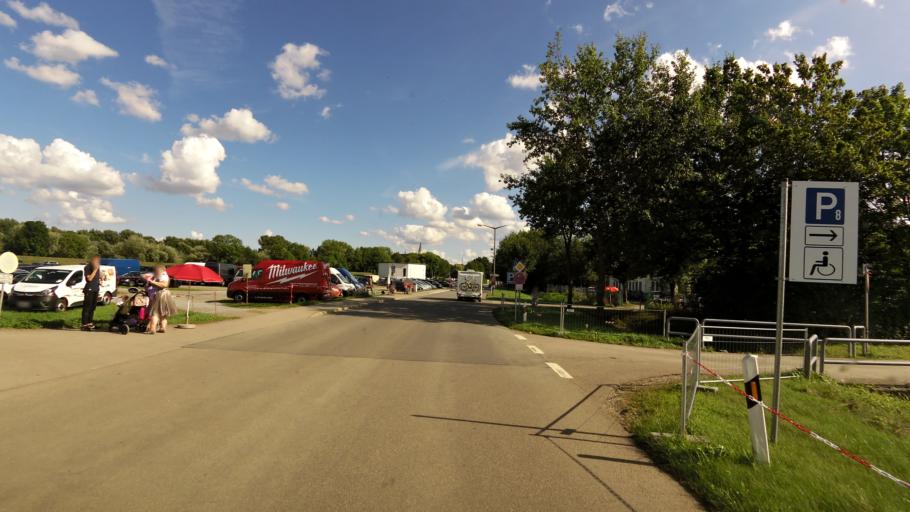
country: DE
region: Bavaria
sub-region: Lower Bavaria
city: Straubing
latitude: 48.8897
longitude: 12.5649
